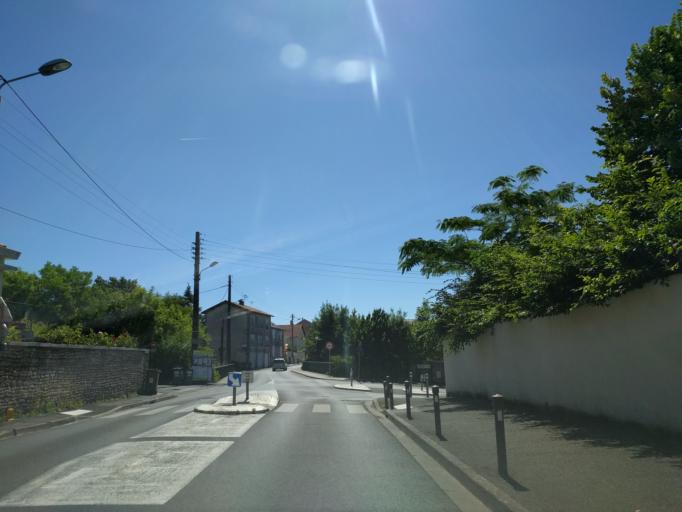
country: FR
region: Poitou-Charentes
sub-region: Departement des Deux-Sevres
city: Niort
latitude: 46.3275
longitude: -0.4449
